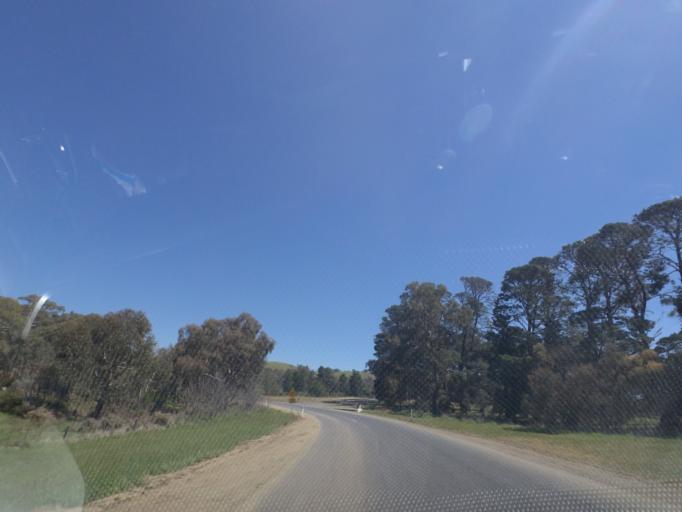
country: AU
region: Victoria
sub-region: Whittlesea
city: Whittlesea
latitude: -37.2890
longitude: 144.9845
